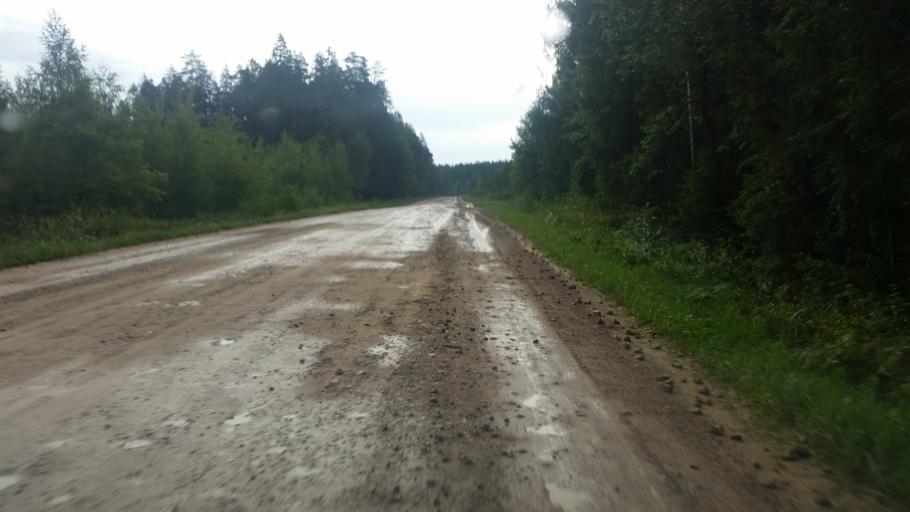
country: LV
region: Vecumnieki
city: Vecumnieki
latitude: 56.4306
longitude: 24.5507
